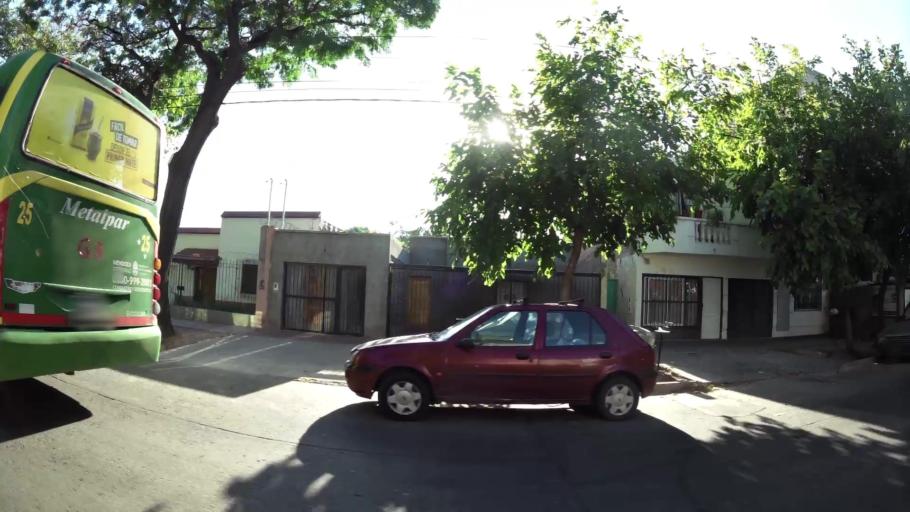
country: AR
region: Mendoza
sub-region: Departamento de Godoy Cruz
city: Godoy Cruz
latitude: -32.9102
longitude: -68.8508
